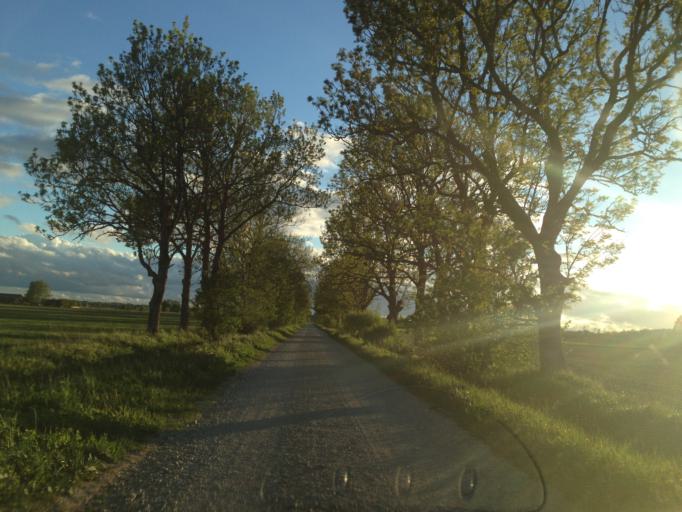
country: EE
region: Raplamaa
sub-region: Maerjamaa vald
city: Marjamaa
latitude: 58.7588
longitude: 24.2032
